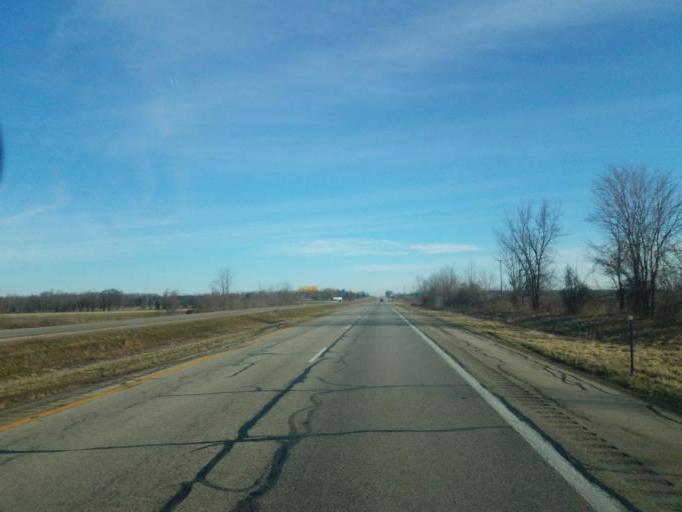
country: US
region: Michigan
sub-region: Gratiot County
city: Ithaca
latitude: 43.2161
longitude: -84.5631
